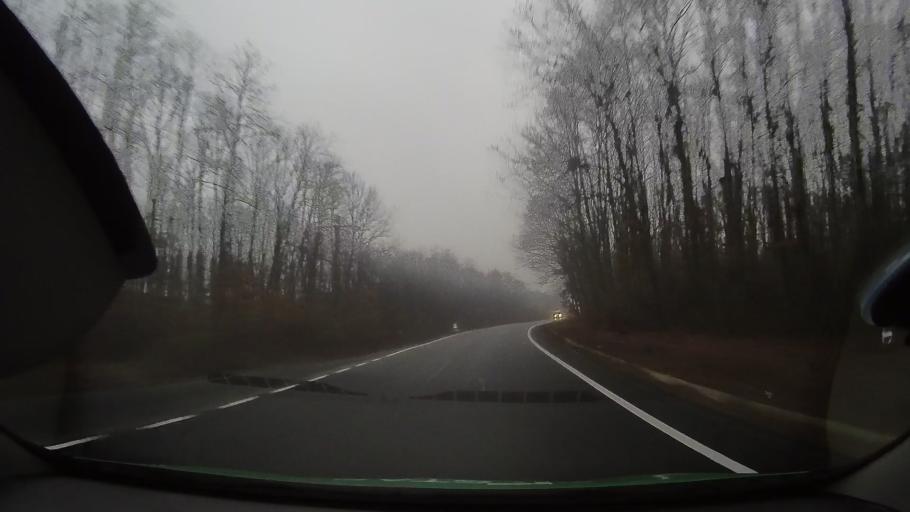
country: RO
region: Bihor
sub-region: Comuna Olcea
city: Olcea
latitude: 46.7002
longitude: 21.9644
